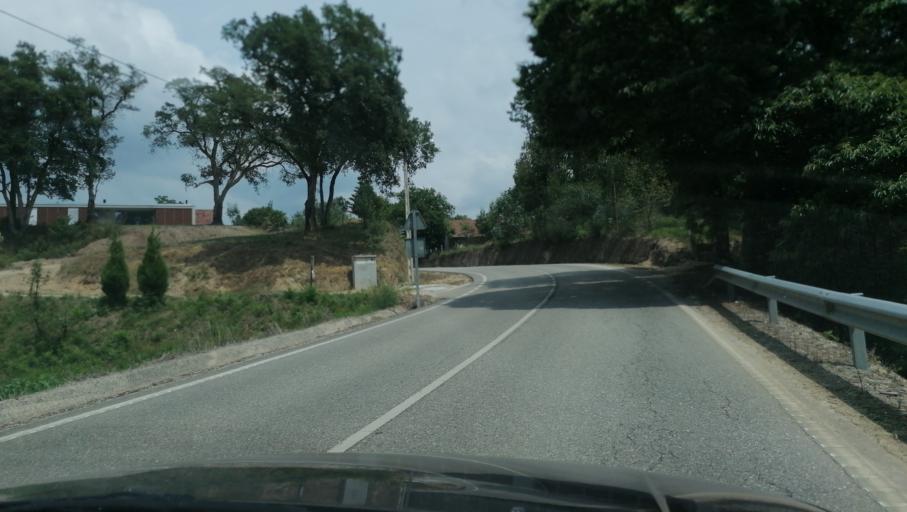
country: ES
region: Galicia
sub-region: Provincia de Pontevedra
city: Tomino
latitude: 42.0147
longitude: -8.7042
